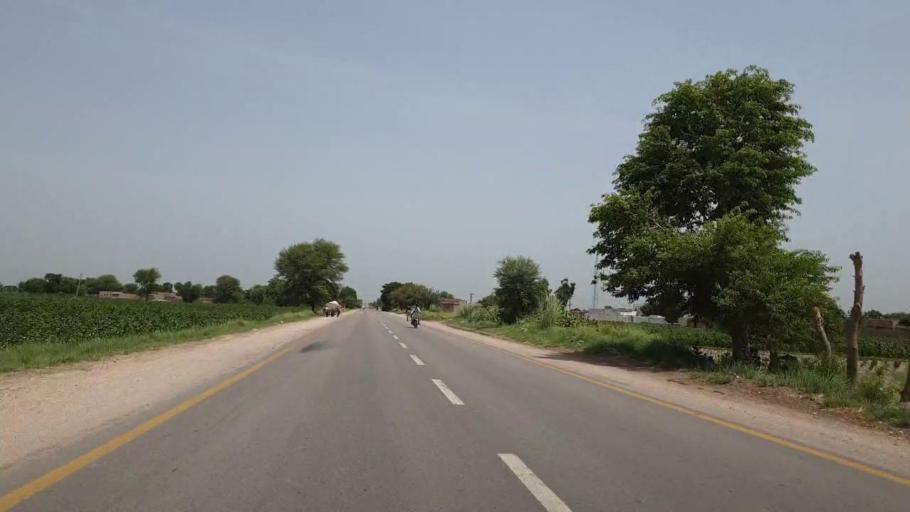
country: PK
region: Sindh
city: Shahpur Chakar
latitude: 26.1550
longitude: 68.6338
